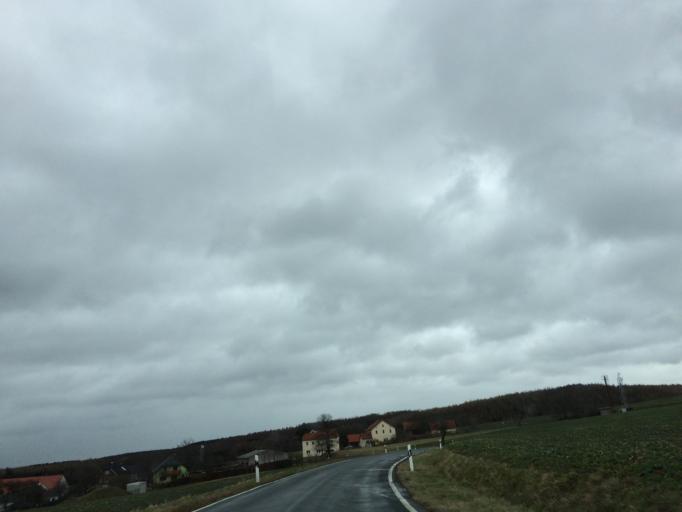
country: DE
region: Thuringia
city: Quaschwitz
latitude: 50.6804
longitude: 11.6988
